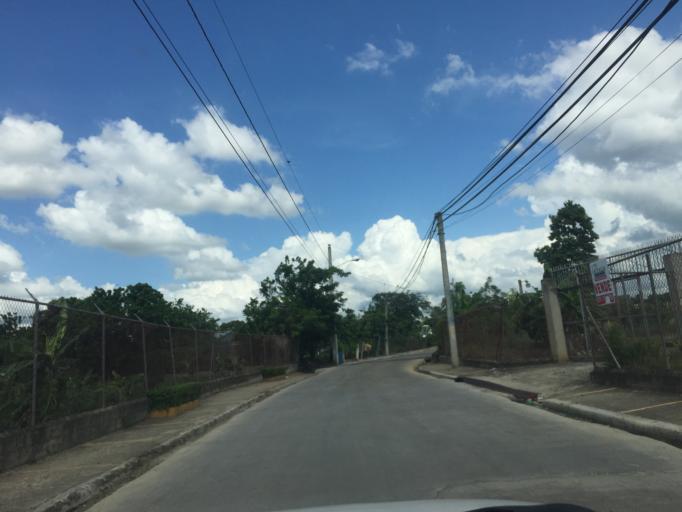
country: DO
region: Santiago
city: Licey al Medio
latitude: 19.3822
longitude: -70.6037
